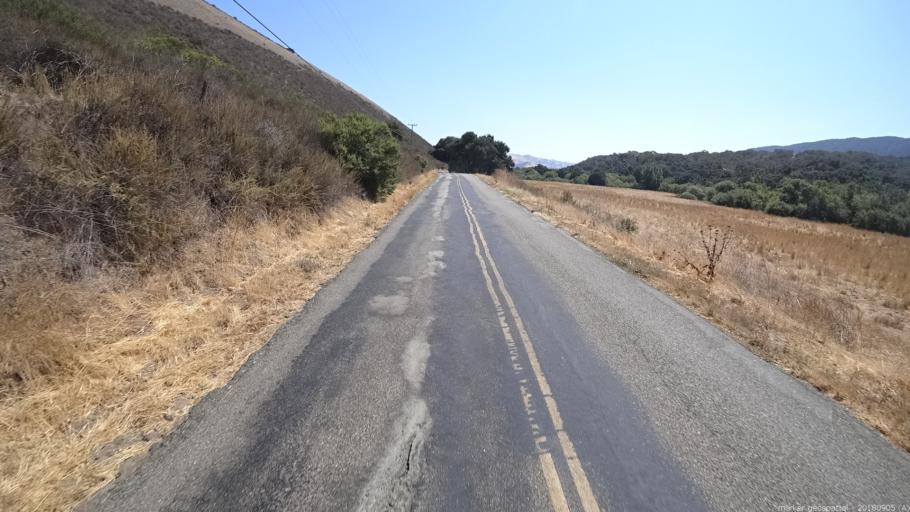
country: US
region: California
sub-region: Monterey County
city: Carmel Valley Village
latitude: 36.4437
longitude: -121.6626
